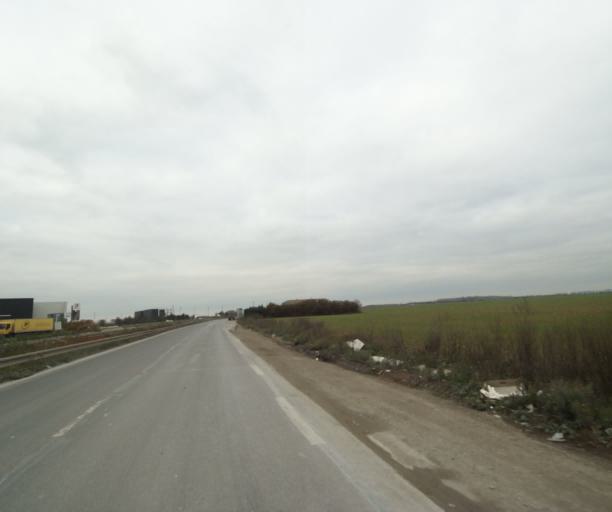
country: FR
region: Ile-de-France
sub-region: Departement du Val-d'Oise
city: Gonesse
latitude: 48.9664
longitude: 2.4673
